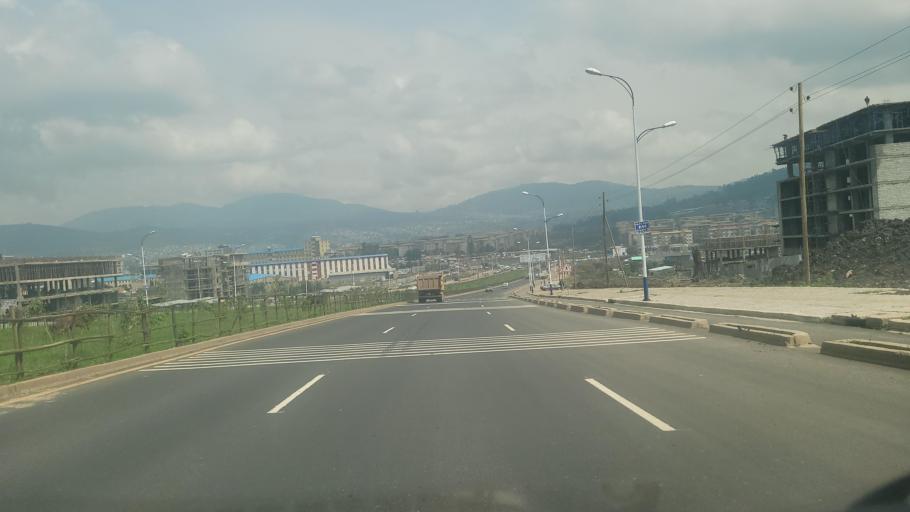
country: ET
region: Adis Abeba
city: Addis Ababa
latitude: 8.9513
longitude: 38.7010
